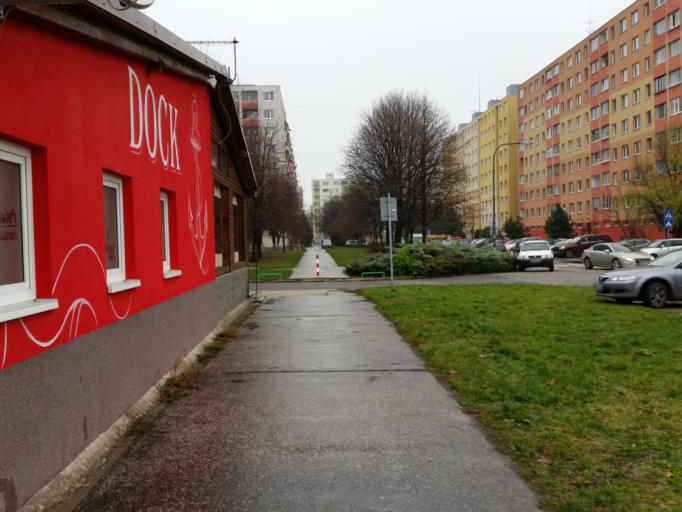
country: SK
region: Bratislavsky
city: Bratislava
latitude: 48.1274
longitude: 17.1063
